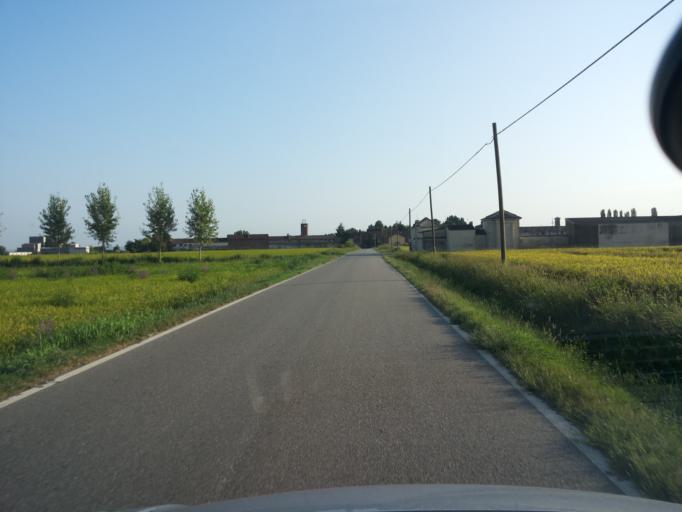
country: IT
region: Piedmont
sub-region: Provincia di Vercelli
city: Sali Vercellese
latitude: 45.3137
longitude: 8.3307
